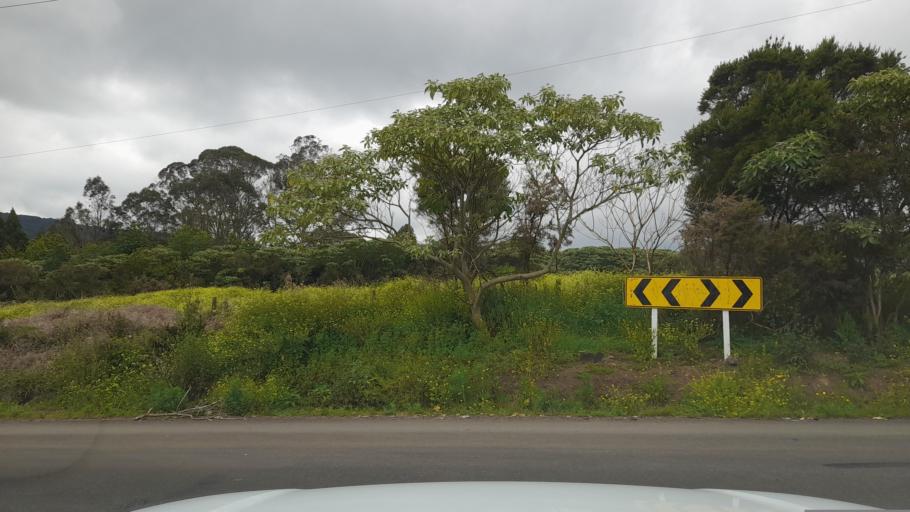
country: NZ
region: Northland
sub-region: Far North District
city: Waimate North
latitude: -35.4025
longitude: 173.7868
